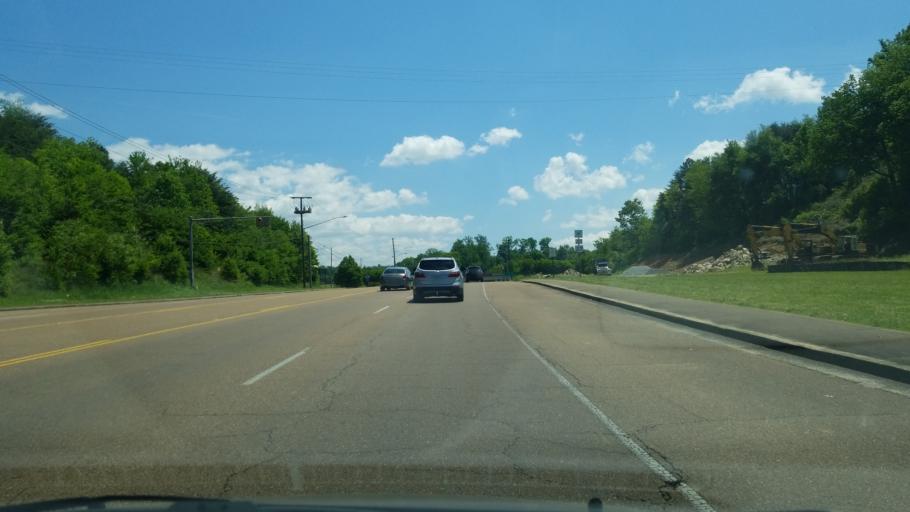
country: US
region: Tennessee
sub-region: Hamilton County
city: Red Bank
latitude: 35.1239
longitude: -85.2998
